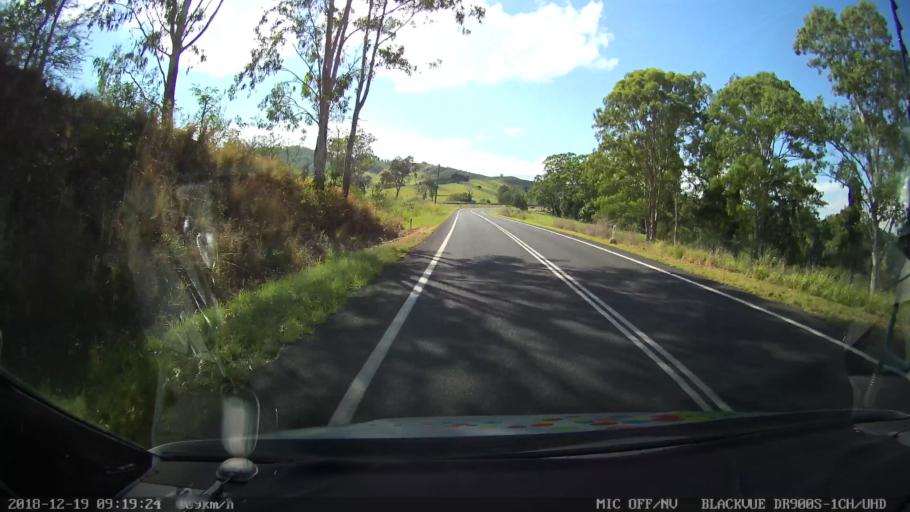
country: AU
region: New South Wales
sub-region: Kyogle
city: Kyogle
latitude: -28.5598
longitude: 152.9770
